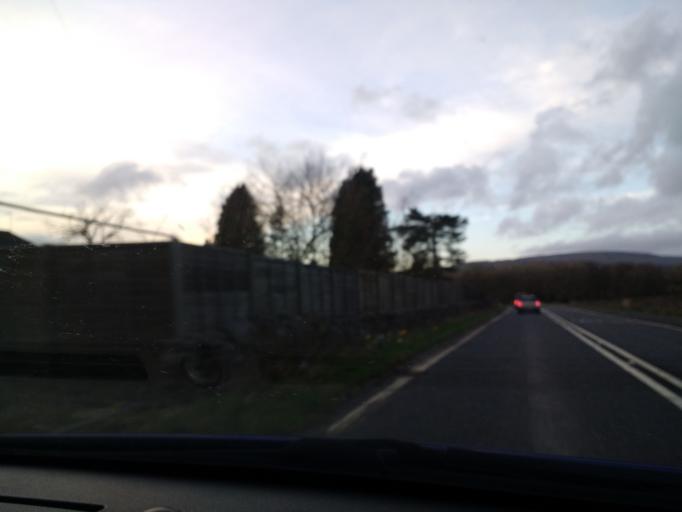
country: GB
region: England
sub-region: North Yorkshire
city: Ingleton
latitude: 54.1436
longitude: -2.4638
